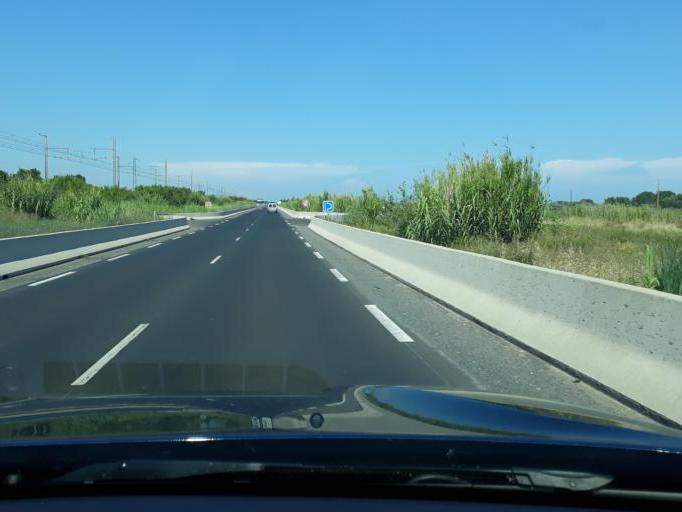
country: FR
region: Languedoc-Roussillon
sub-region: Departement de l'Herault
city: Marseillan
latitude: 43.3252
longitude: 3.5504
